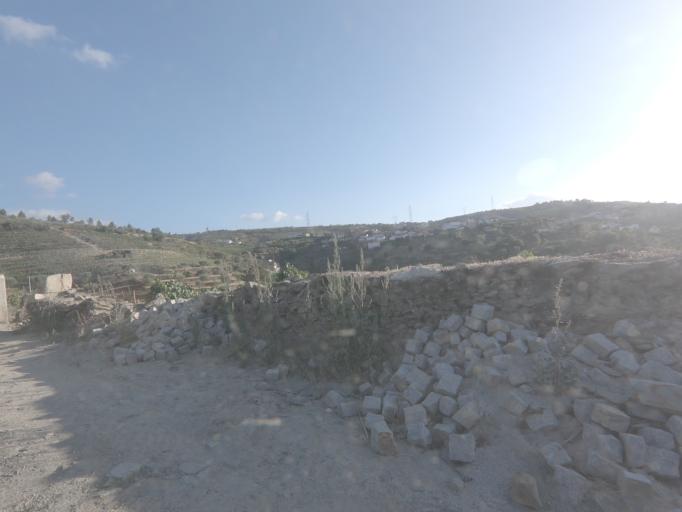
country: PT
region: Viseu
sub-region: Tabuaco
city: Tabuaco
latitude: 41.1490
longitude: -7.6031
